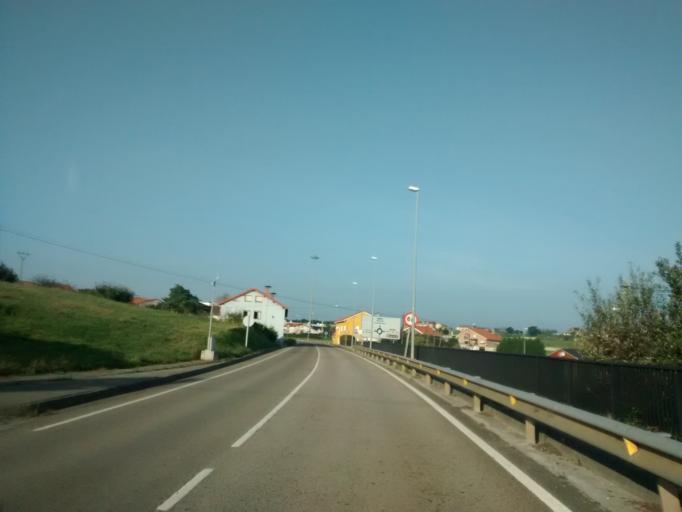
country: ES
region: Cantabria
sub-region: Provincia de Cantabria
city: Miengo
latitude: 43.4270
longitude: -3.9659
